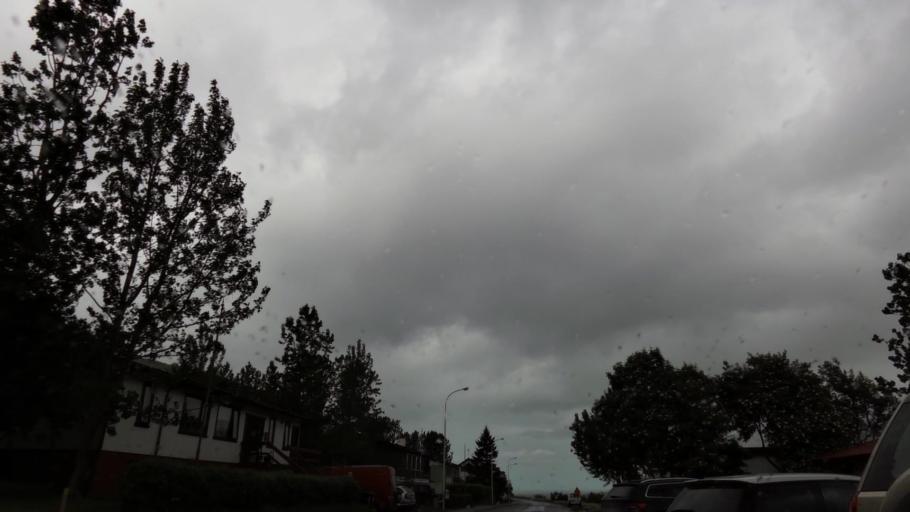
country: IS
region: Westfjords
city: Isafjoerdur
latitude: 65.8790
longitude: -23.4983
